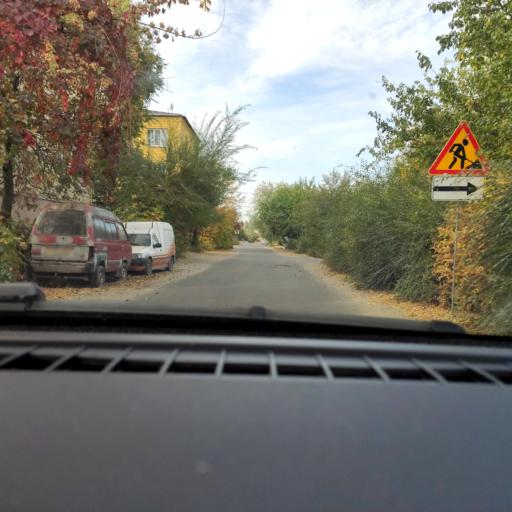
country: RU
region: Voronezj
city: Voronezh
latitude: 51.6906
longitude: 39.1595
